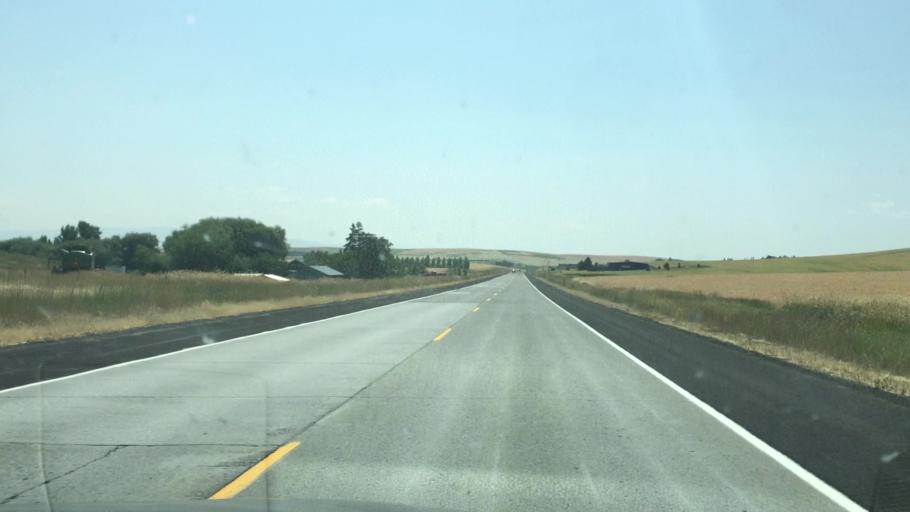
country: US
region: Idaho
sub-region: Lewis County
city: Nezperce
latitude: 46.0840
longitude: -116.3454
